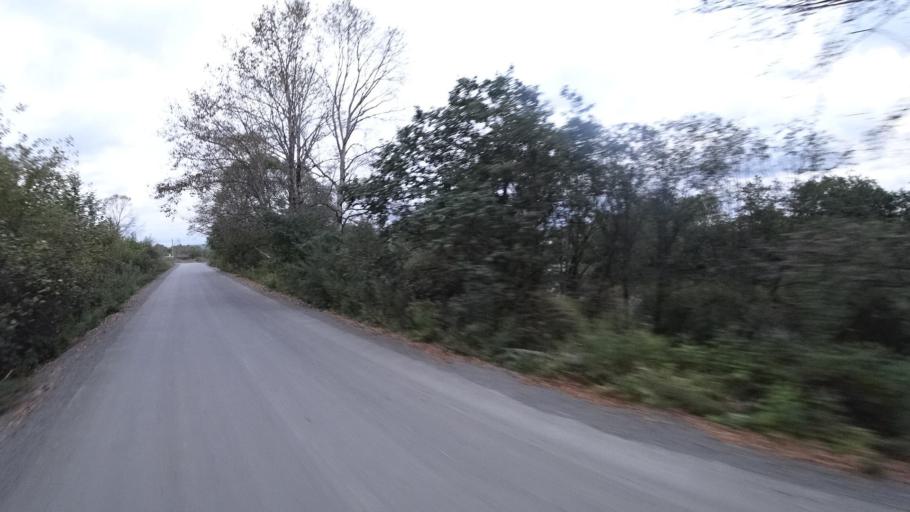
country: RU
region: Jewish Autonomous Oblast
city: Izvestkovyy
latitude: 48.9925
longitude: 131.5408
